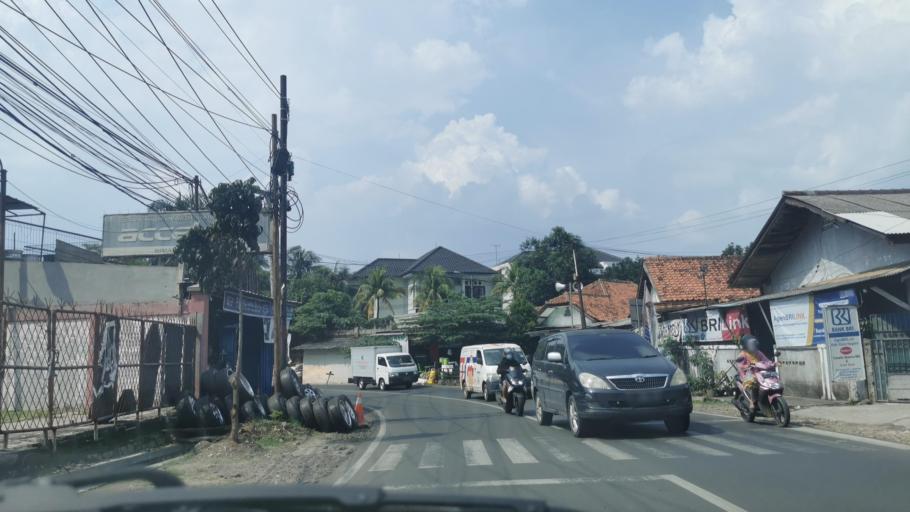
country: ID
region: West Java
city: Depok
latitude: -6.4070
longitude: 106.8359
